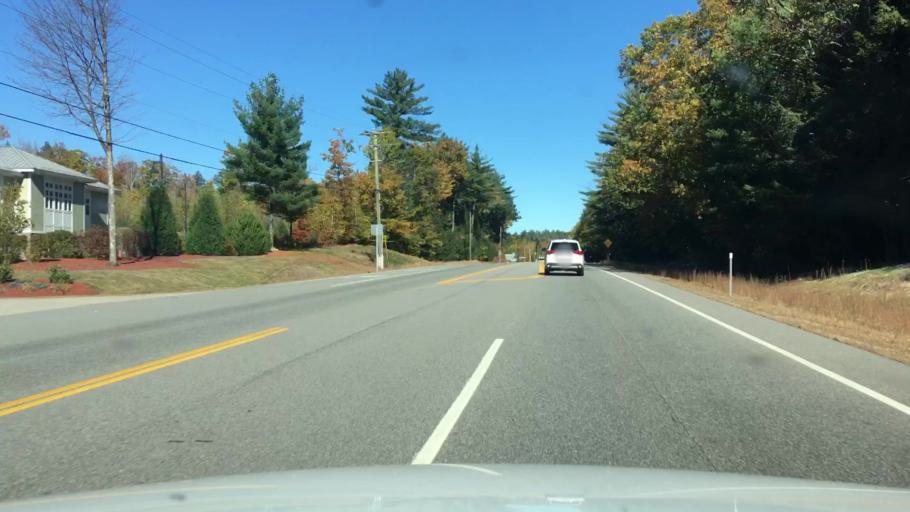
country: US
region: New Hampshire
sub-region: Carroll County
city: Sanbornville
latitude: 43.5537
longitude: -71.0404
